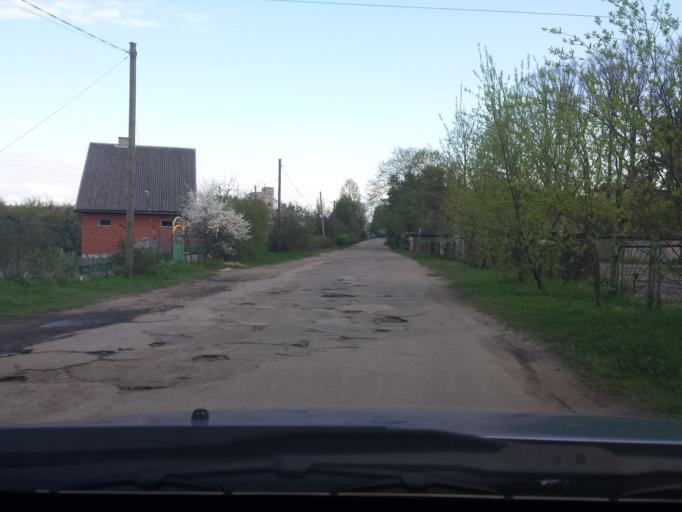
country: LV
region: Riga
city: Jaunciems
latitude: 56.9976
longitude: 24.2242
